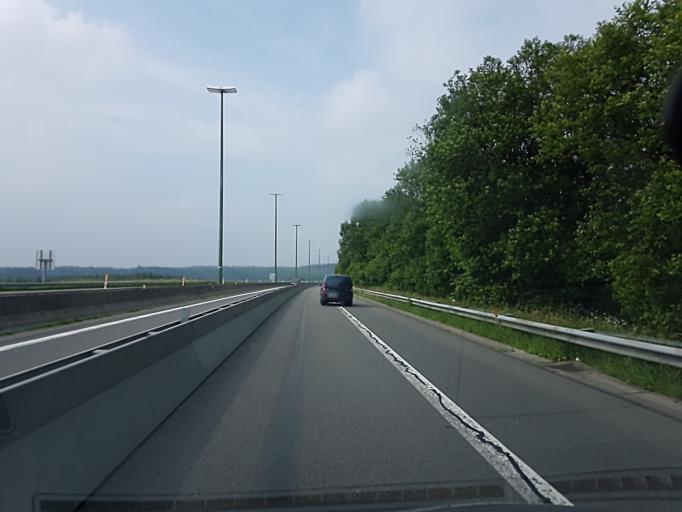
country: BE
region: Wallonia
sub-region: Province de Liege
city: Ferrieres
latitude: 50.3686
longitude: 5.6719
